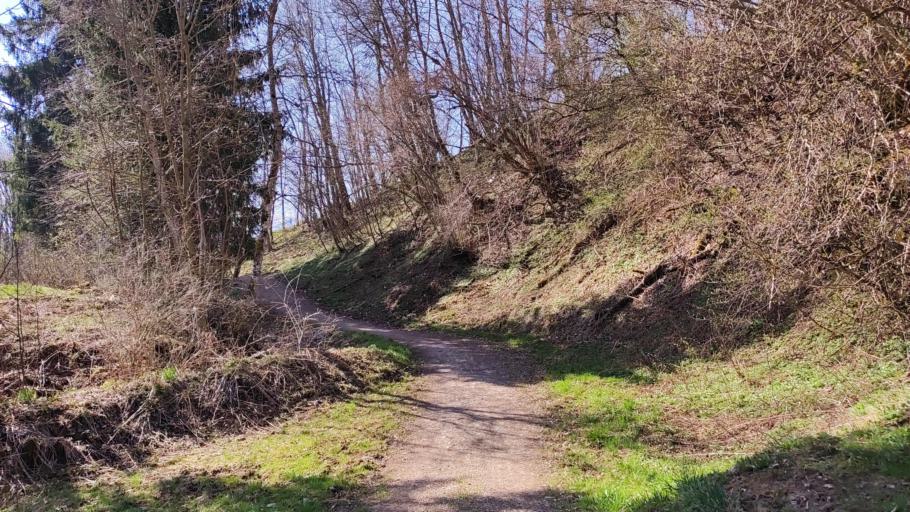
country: DE
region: Bavaria
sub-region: Upper Bavaria
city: Unterammergau
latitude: 47.6277
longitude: 11.0353
